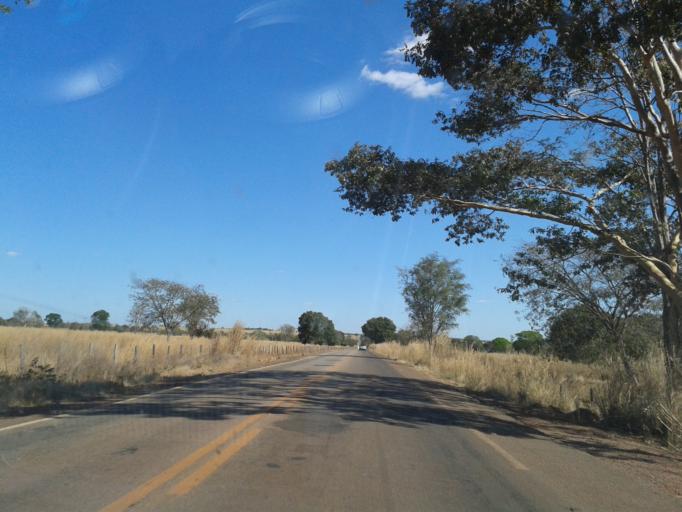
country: BR
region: Goias
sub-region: Crixas
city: Crixas
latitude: -14.1215
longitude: -50.3472
